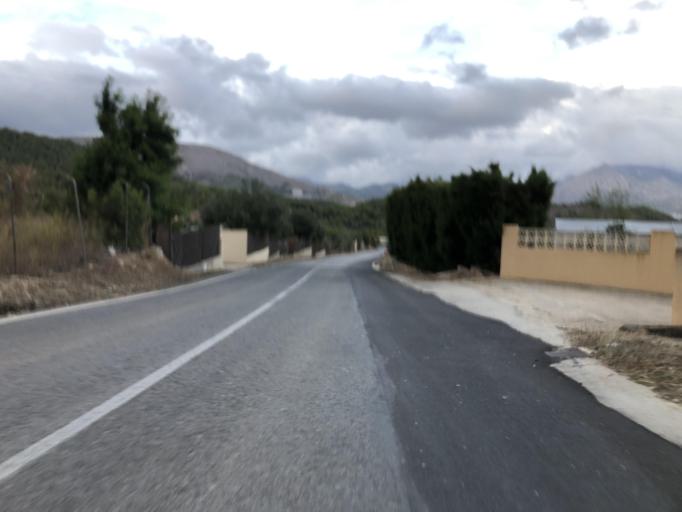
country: ES
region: Valencia
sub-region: Provincia de Alicante
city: Polop
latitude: 38.6306
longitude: -0.1472
